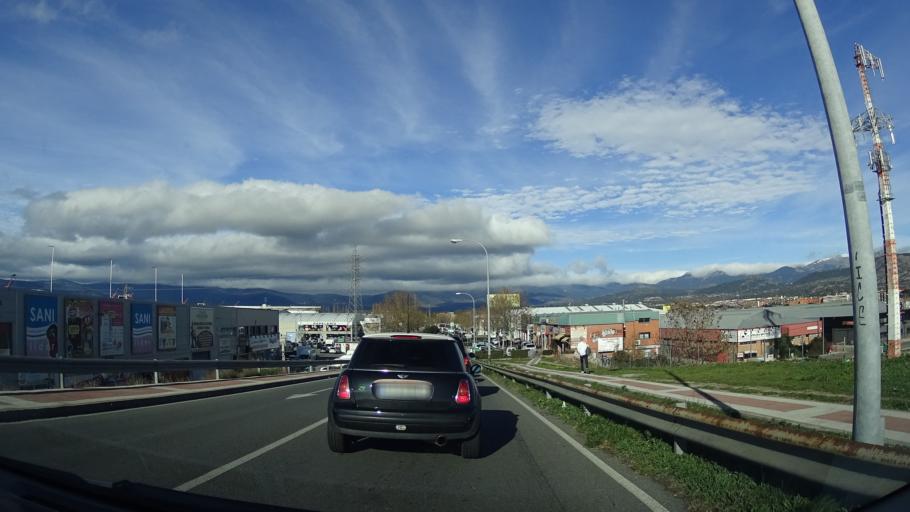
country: ES
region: Madrid
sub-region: Provincia de Madrid
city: Collado-Villalba
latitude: 40.6253
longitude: -4.0166
